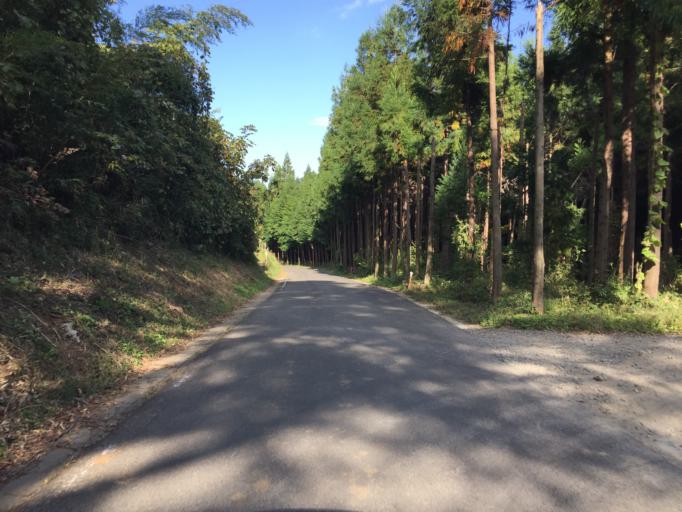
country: JP
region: Fukushima
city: Nihommatsu
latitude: 37.6696
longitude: 140.4263
